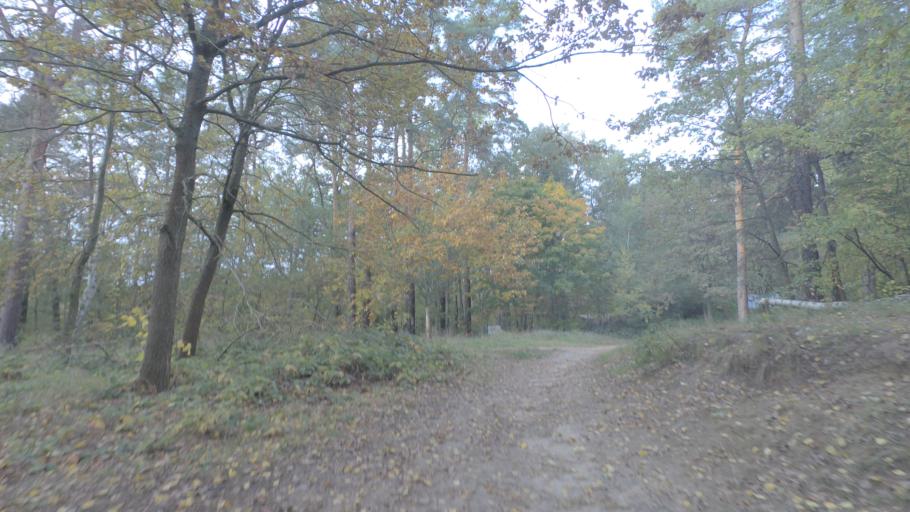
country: DE
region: Brandenburg
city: Ludwigsfelde
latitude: 52.3056
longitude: 13.2382
